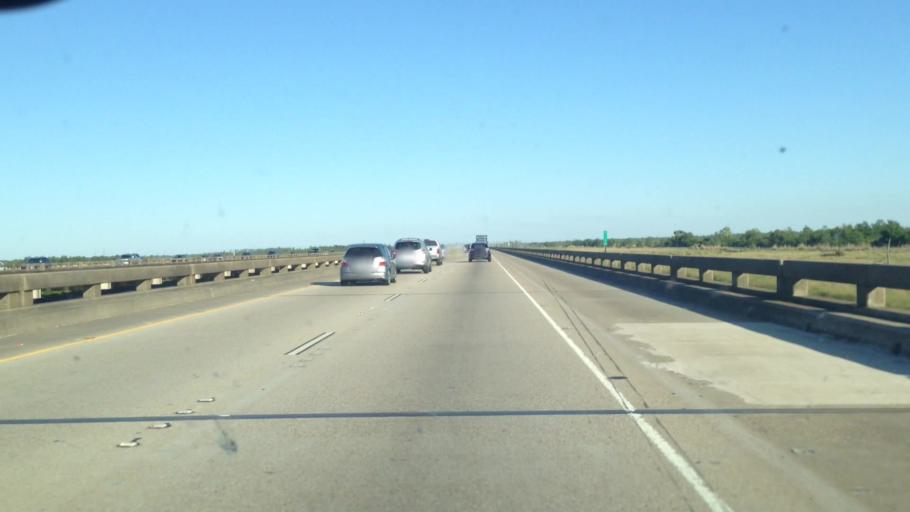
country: US
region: Louisiana
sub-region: Saint Charles Parish
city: Ama
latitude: 30.0220
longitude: -90.3227
